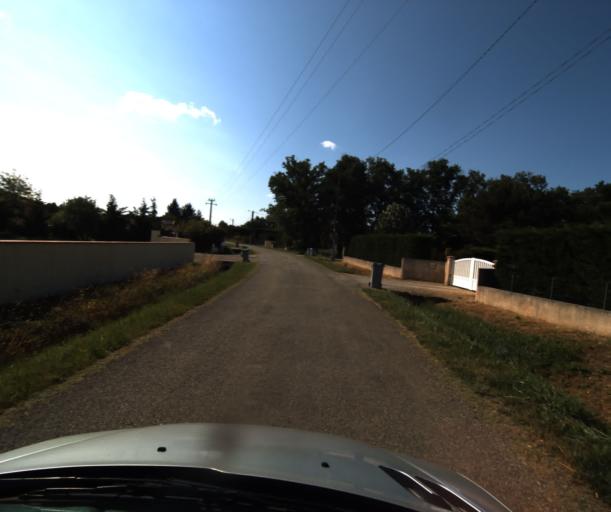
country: FR
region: Midi-Pyrenees
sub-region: Departement du Tarn-et-Garonne
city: Campsas
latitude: 43.9353
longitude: 1.3060
